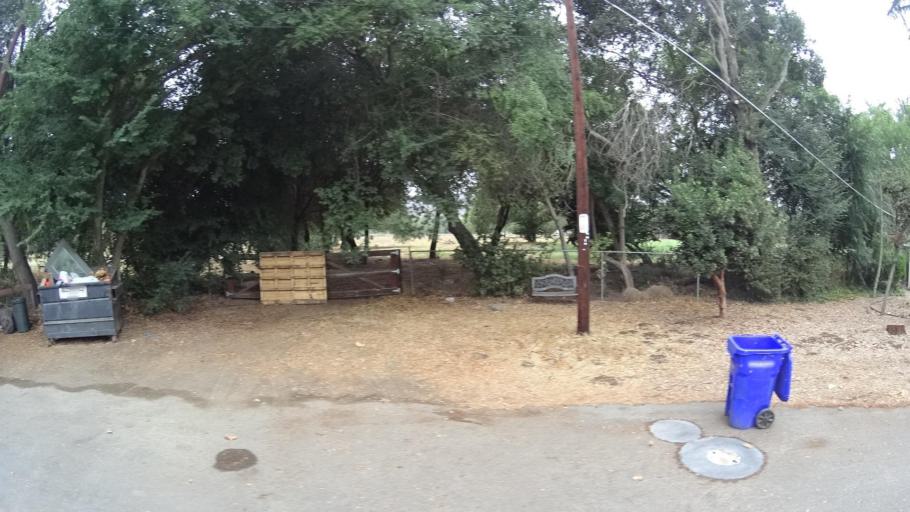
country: US
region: California
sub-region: San Diego County
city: Escondido
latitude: 33.1194
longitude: -117.1298
